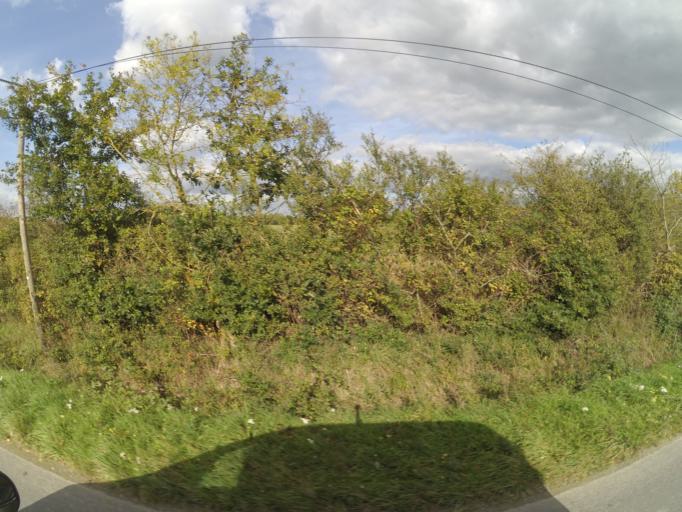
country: FR
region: Pays de la Loire
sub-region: Departement de la Loire-Atlantique
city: Casson
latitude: 47.4006
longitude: -1.5774
